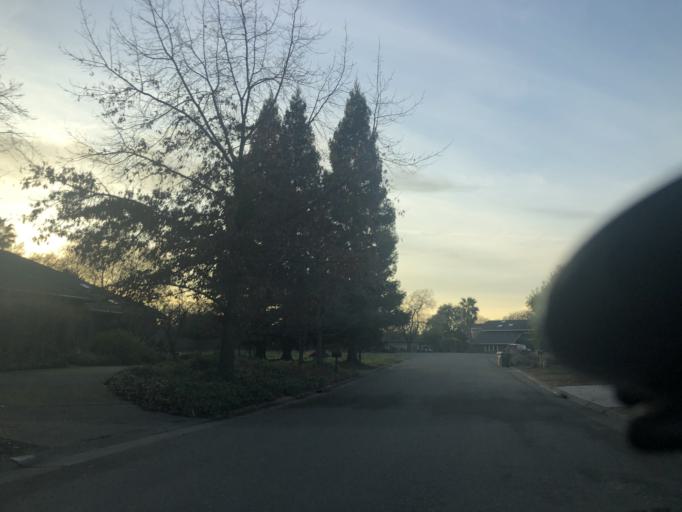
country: US
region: California
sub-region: Sacramento County
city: Gold River
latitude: 38.6378
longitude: -121.2271
